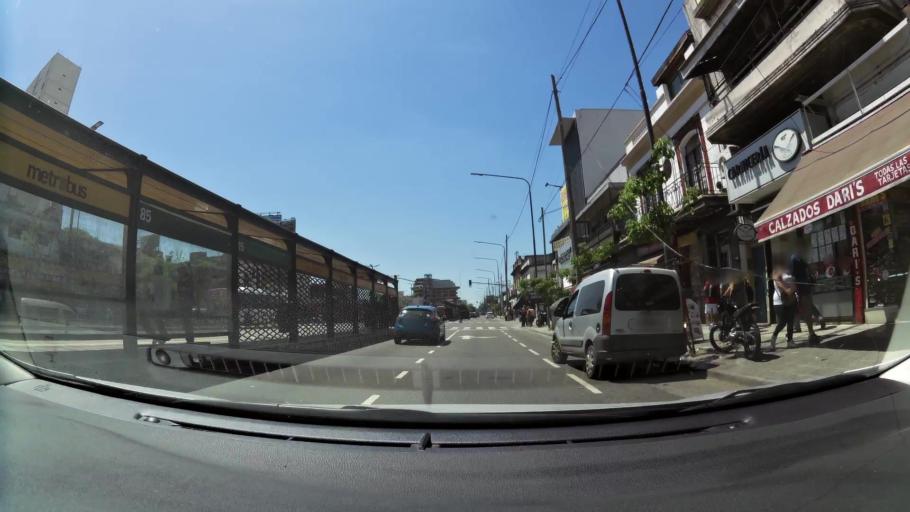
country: AR
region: Buenos Aires
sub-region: Partido de Avellaneda
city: Avellaneda
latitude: -34.6513
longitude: -58.4162
